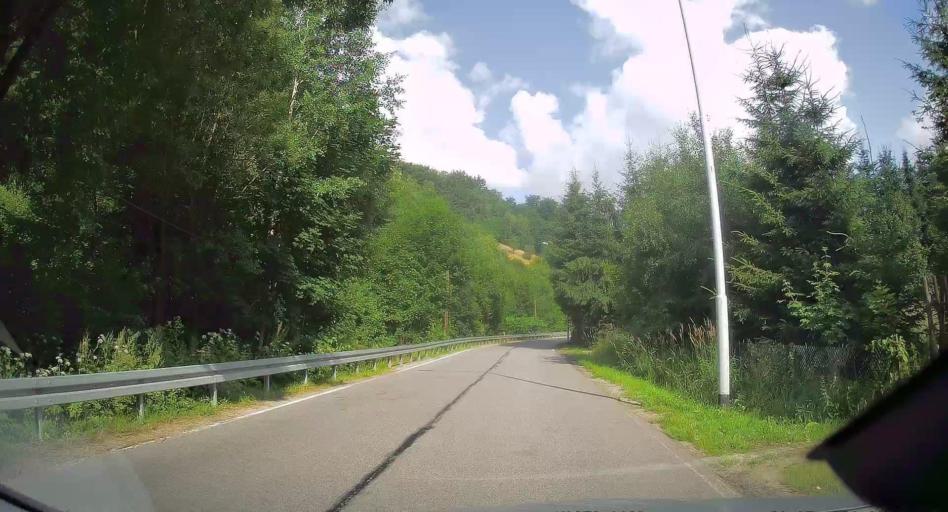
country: PL
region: Lower Silesian Voivodeship
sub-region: Powiat walbrzyski
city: Walim
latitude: 50.6802
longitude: 16.4408
